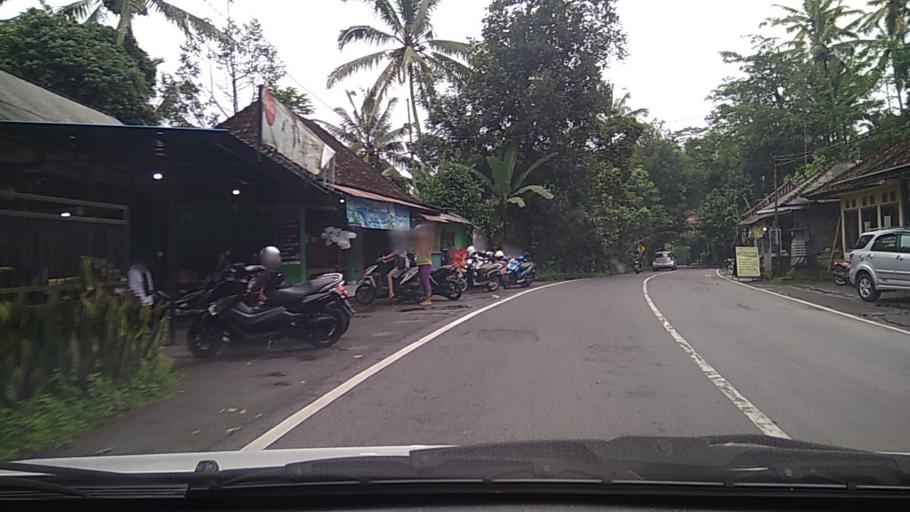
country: ID
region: Bali
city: Banjar Manukayaanyar
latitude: -8.4178
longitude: 115.3134
